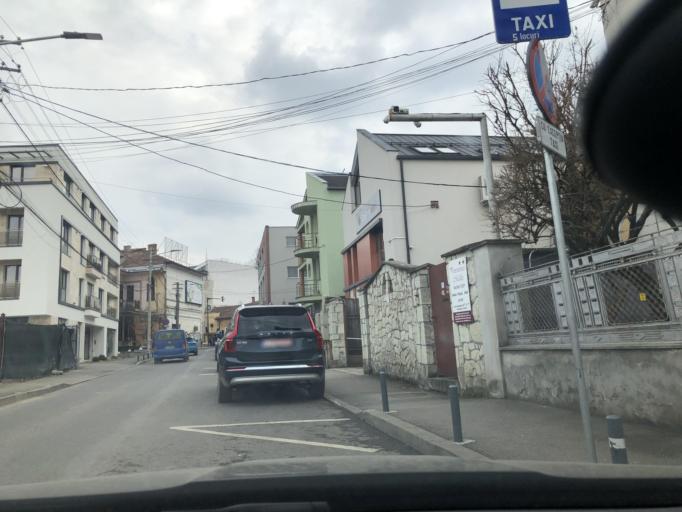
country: RO
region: Cluj
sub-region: Municipiul Cluj-Napoca
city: Cluj-Napoca
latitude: 46.7647
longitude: 23.5731
